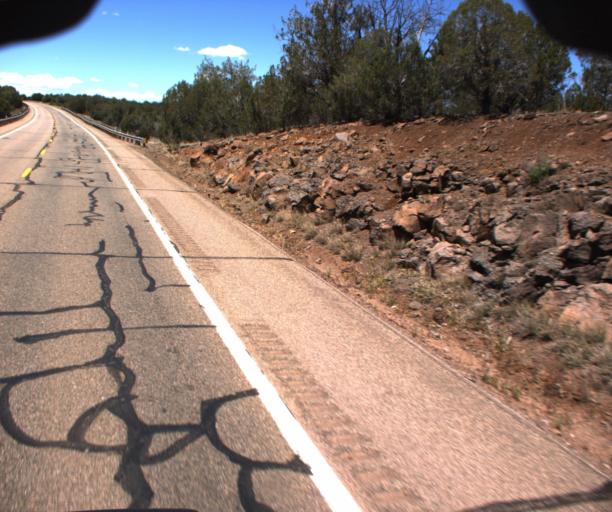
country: US
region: Arizona
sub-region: Yavapai County
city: Paulden
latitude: 35.0842
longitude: -112.4073
